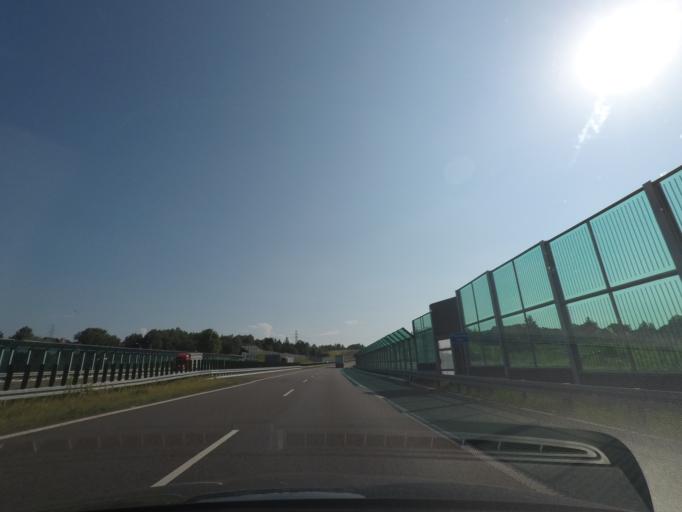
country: PL
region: Silesian Voivodeship
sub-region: Powiat wodzislawski
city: Mszana
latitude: 49.9662
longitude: 18.5353
